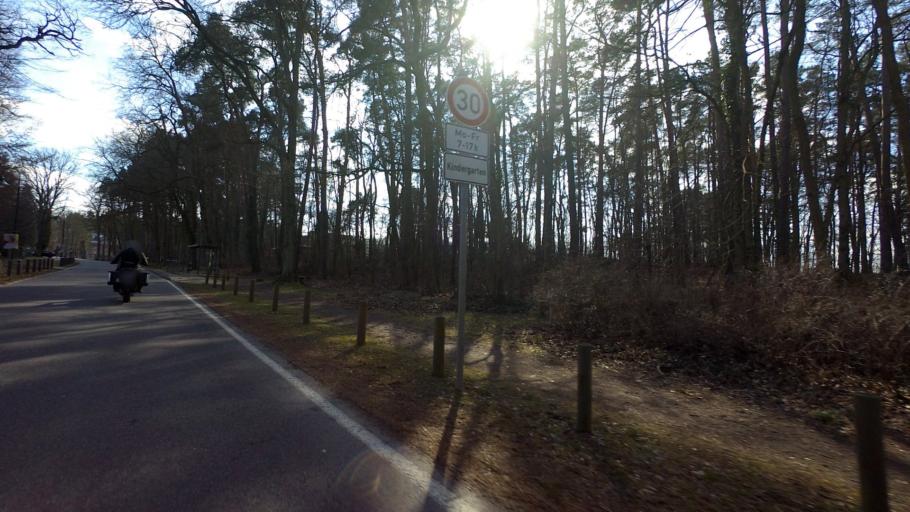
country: DE
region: Brandenburg
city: Biesenthal
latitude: 52.7736
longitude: 13.6144
